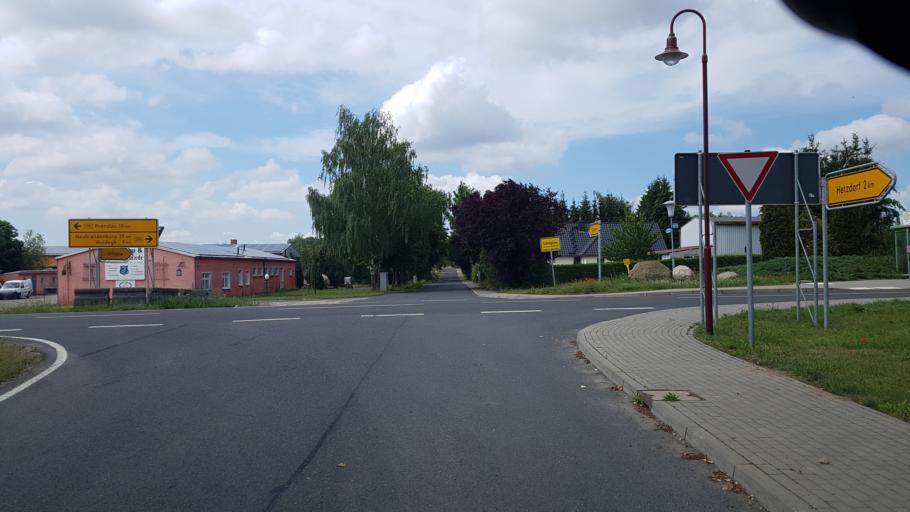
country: DE
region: Mecklenburg-Vorpommern
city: Strasburg
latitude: 53.4259
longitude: 13.6952
